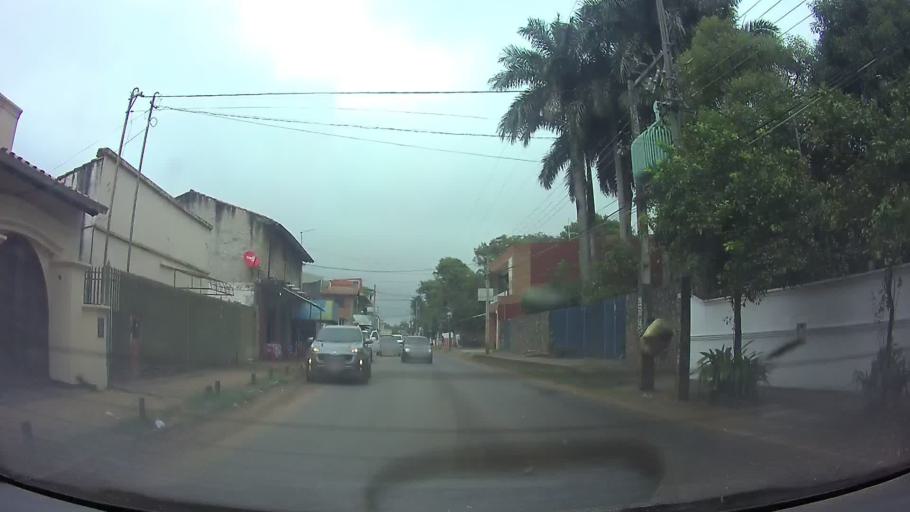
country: PY
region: Central
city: San Lorenzo
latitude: -25.3342
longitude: -57.5076
